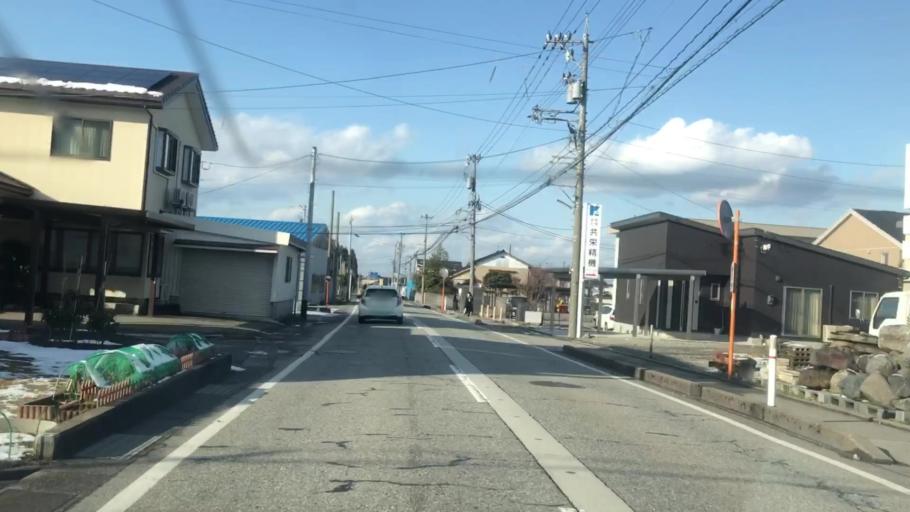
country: JP
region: Toyama
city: Toyama-shi
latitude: 36.6817
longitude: 137.2728
